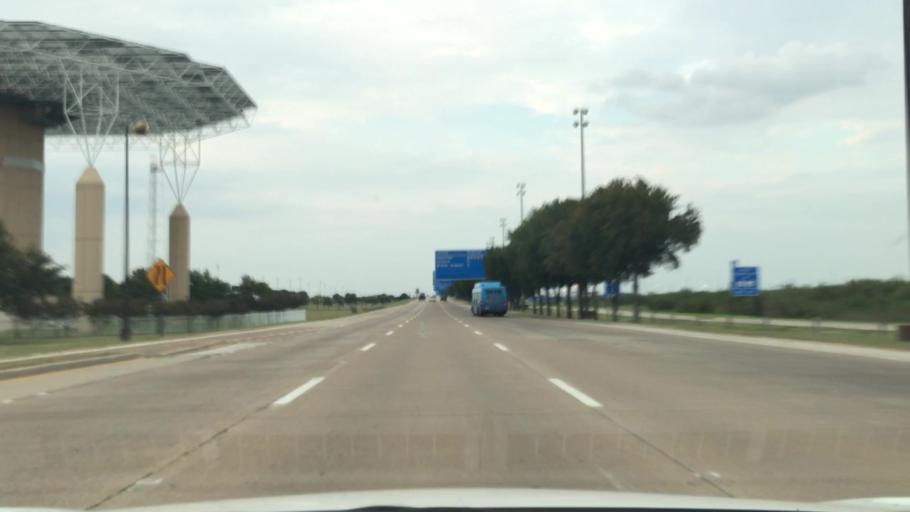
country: US
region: Texas
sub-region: Tarrant County
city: Euless
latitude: 32.8682
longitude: -97.0400
